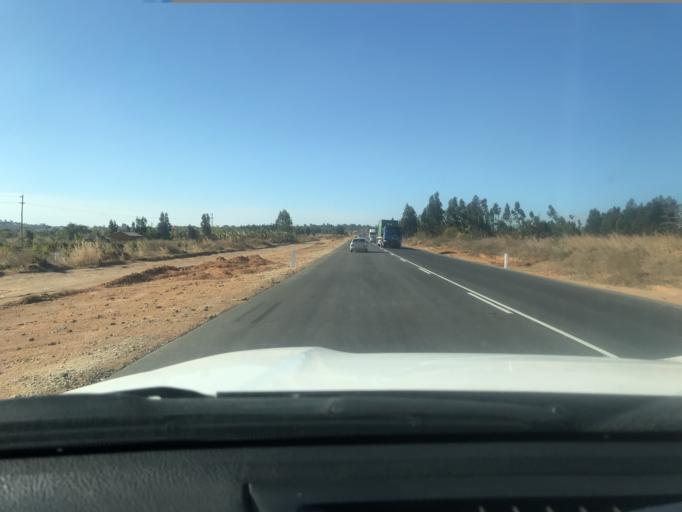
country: TZ
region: Iringa
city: Malangali
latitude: -8.6521
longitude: 34.9473
